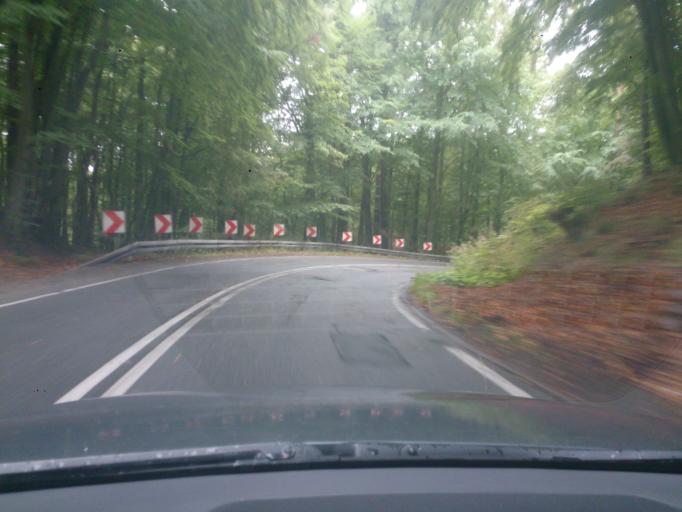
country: PL
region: Pomeranian Voivodeship
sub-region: Gdynia
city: Wielki Kack
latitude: 54.4599
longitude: 18.5089
